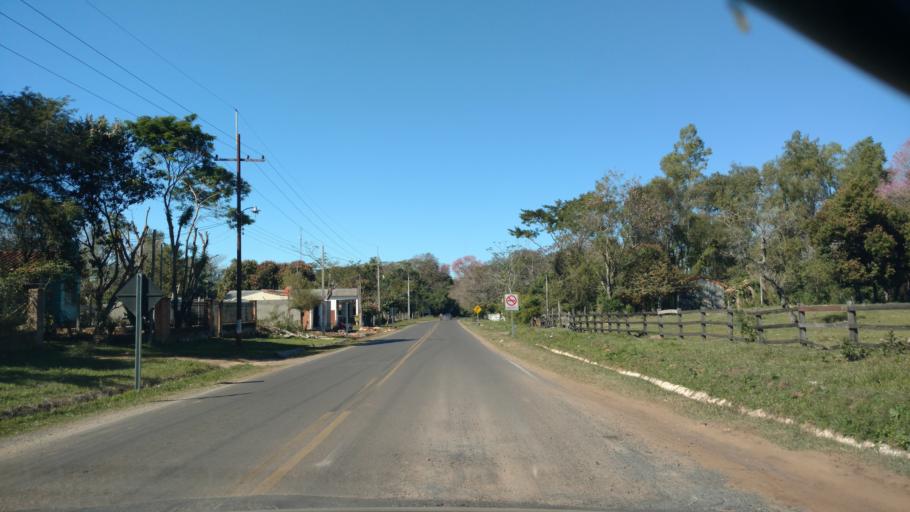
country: PY
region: Central
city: Ypacarai
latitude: -25.4307
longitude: -57.2856
